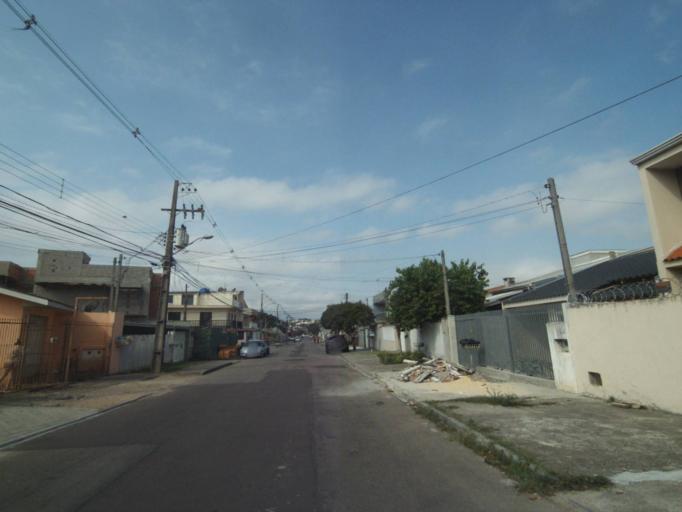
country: BR
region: Parana
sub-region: Sao Jose Dos Pinhais
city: Sao Jose dos Pinhais
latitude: -25.5368
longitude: -49.2585
